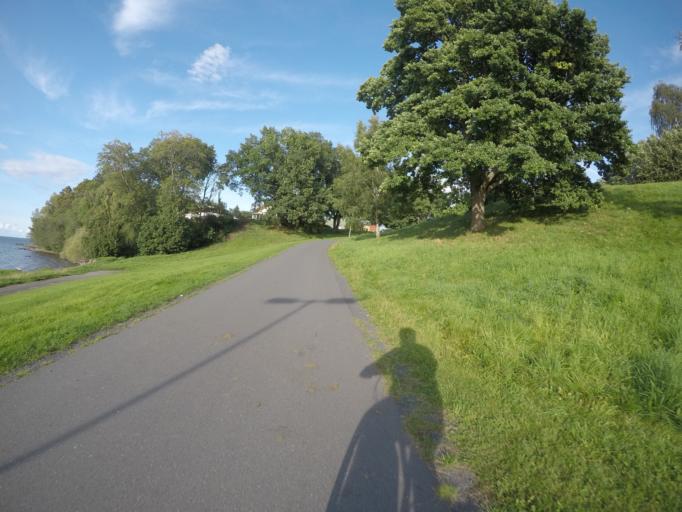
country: SE
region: Joenkoeping
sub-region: Jonkopings Kommun
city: Jonkoping
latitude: 57.7835
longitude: 14.2112
